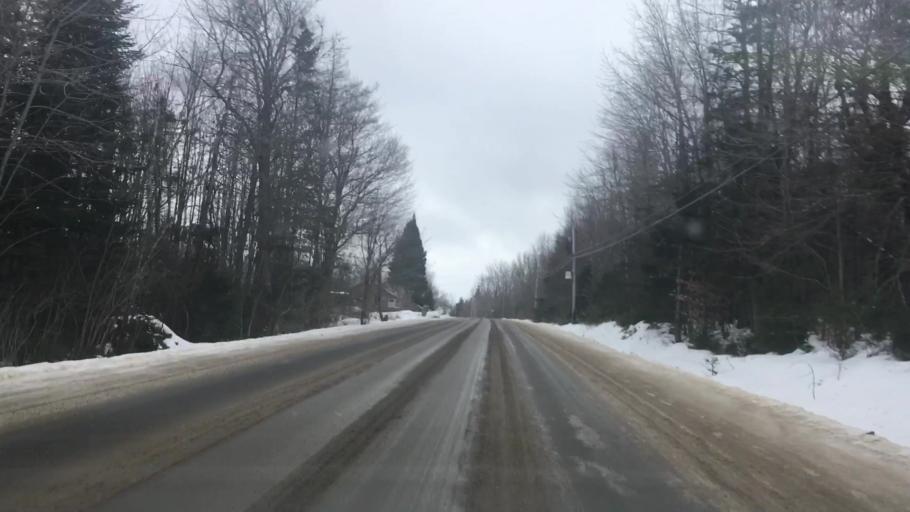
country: US
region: Maine
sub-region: Washington County
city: East Machias
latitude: 44.9882
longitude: -67.4591
